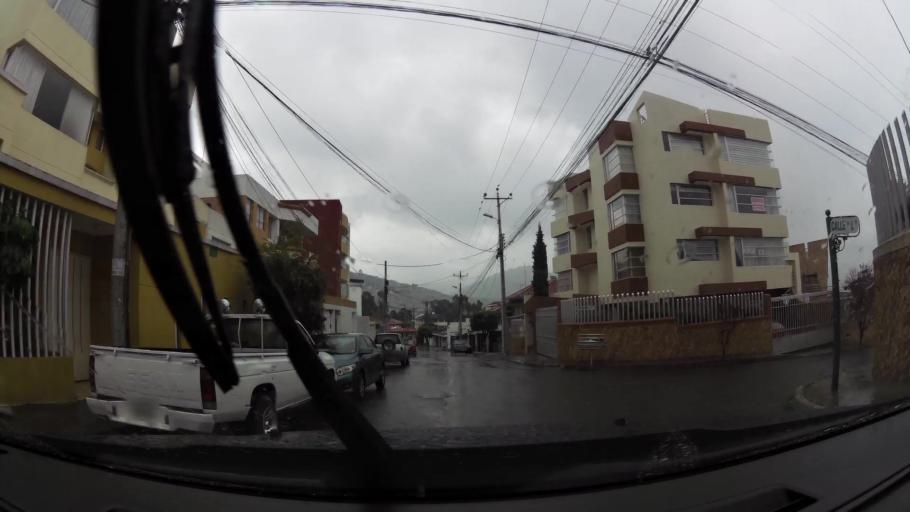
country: EC
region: Pichincha
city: Quito
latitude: -0.1026
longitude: -78.5016
